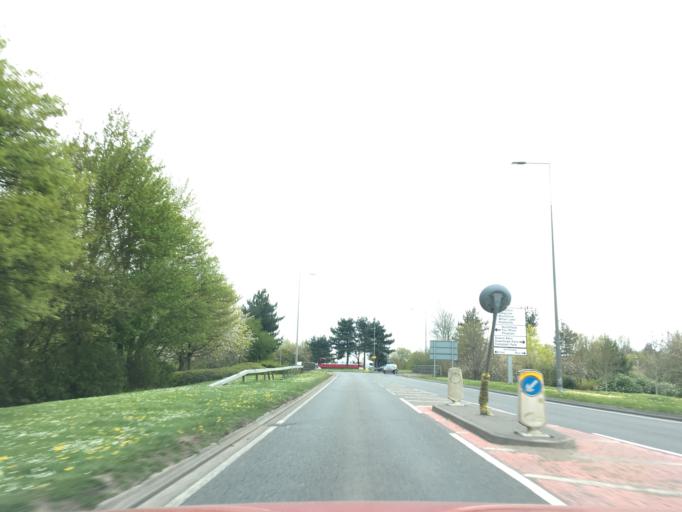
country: GB
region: England
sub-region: Milton Keynes
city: Milton Keynes
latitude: 52.0557
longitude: -0.7284
